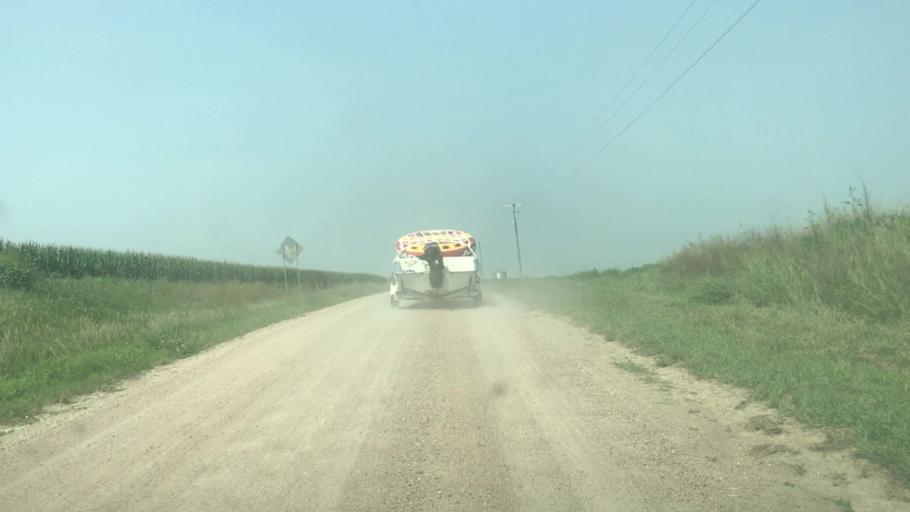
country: US
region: Nebraska
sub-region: Sherman County
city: Loup City
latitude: 41.2648
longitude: -98.9191
